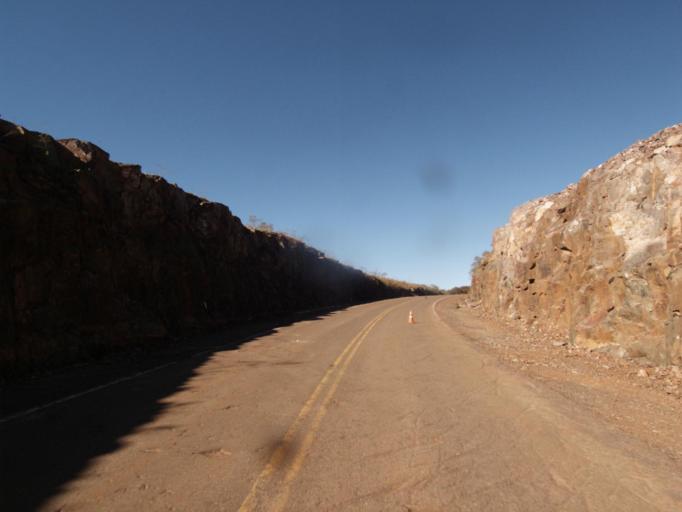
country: AR
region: Misiones
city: Bernardo de Irigoyen
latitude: -26.6130
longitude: -53.7180
